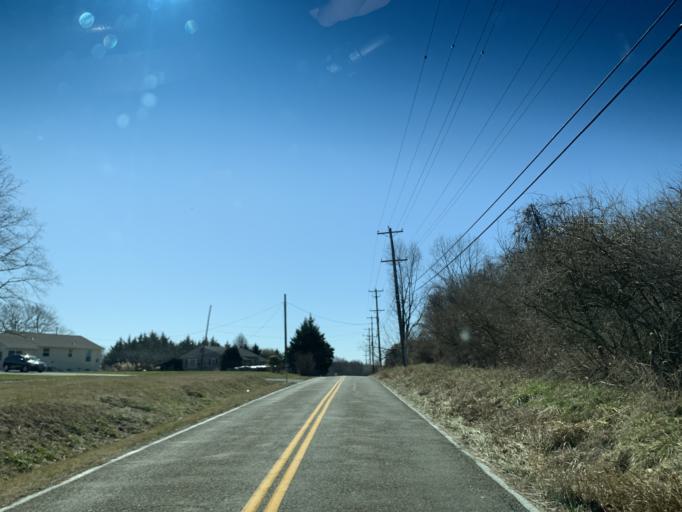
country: US
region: Maryland
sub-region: Cecil County
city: Elkton
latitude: 39.5137
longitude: -75.8268
